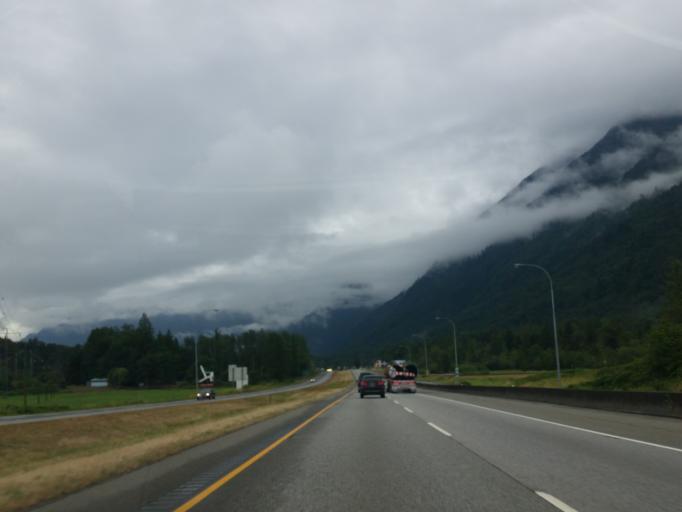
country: CA
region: British Columbia
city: Agassiz
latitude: 49.1819
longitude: -121.7588
